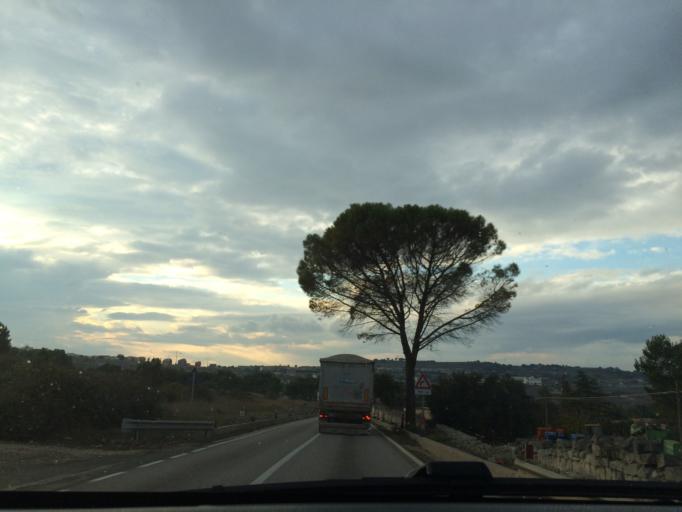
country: IT
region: Basilicate
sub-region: Provincia di Matera
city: Matera
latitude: 40.6809
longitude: 16.6113
